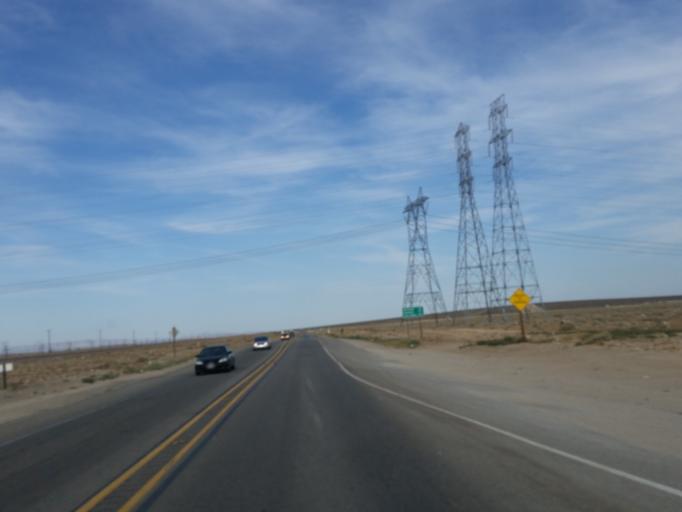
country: US
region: California
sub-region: Kern County
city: Boron
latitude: 34.9919
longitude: -117.5362
